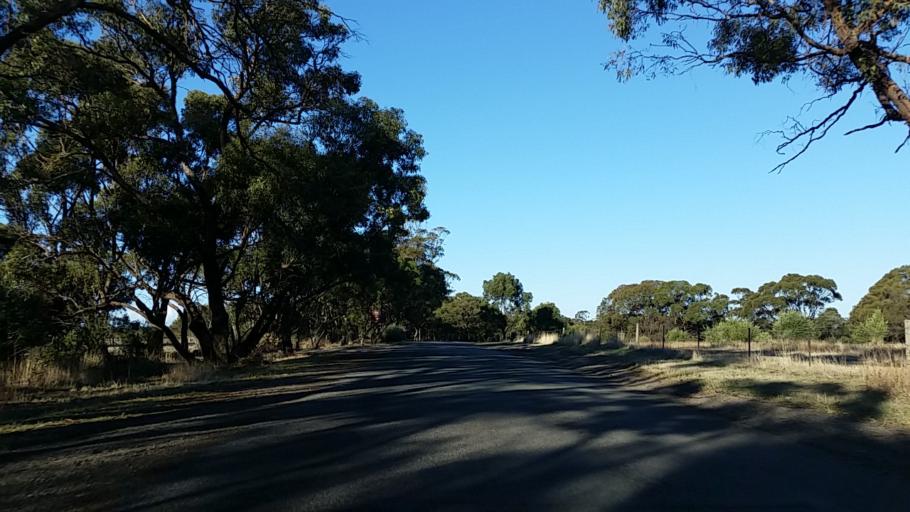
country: AU
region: South Australia
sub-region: Onkaparinga
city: Hackham
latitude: -35.1527
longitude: 138.5562
